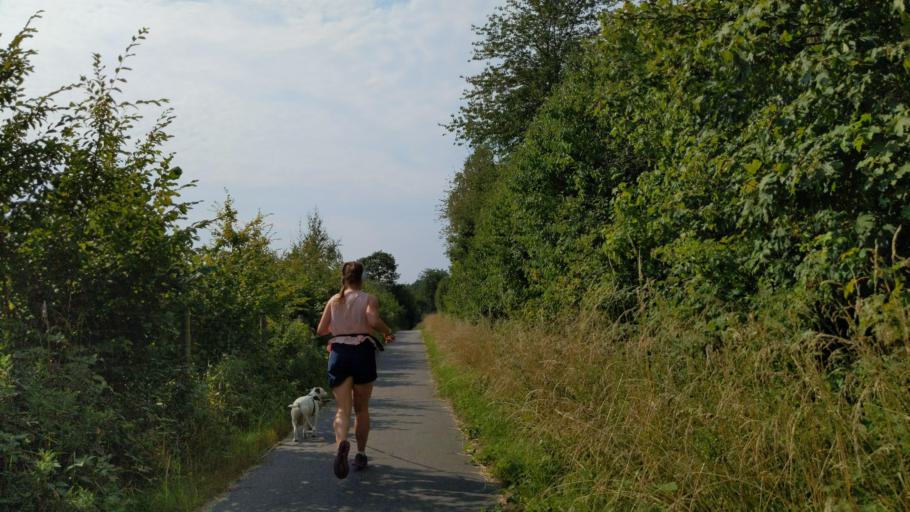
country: DE
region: Schleswig-Holstein
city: Behlendorf
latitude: 53.7031
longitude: 10.6592
